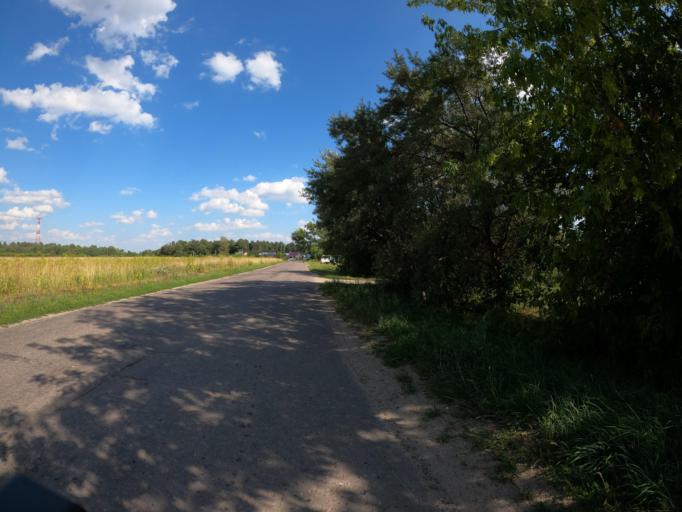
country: RU
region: Moskovskaya
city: Peski
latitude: 55.2218
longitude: 38.7607
